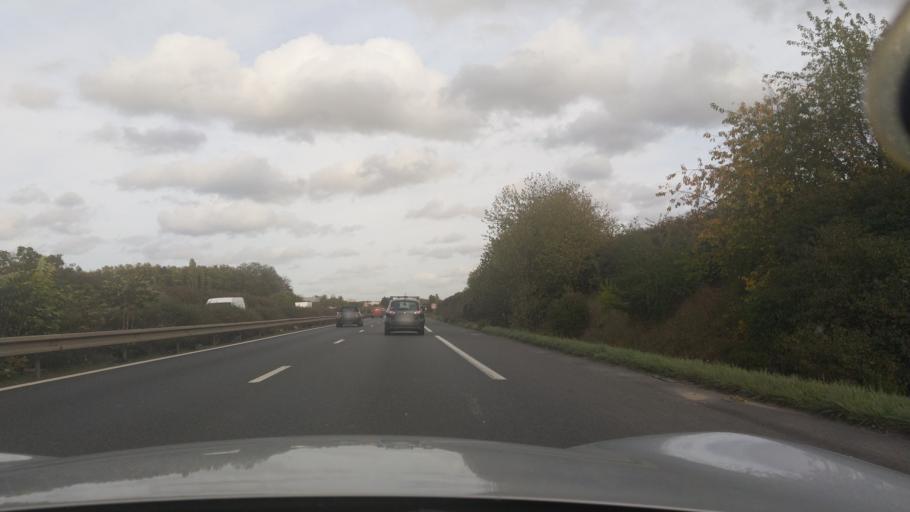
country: FR
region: Ile-de-France
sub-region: Departement du Val-d'Oise
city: Auvers-sur-Oise
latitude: 49.0516
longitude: 2.1533
